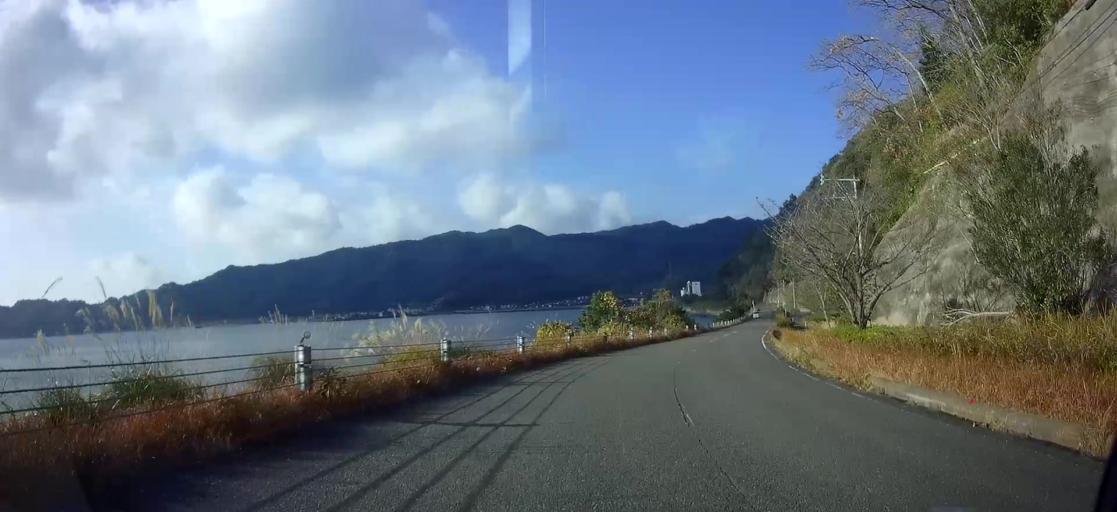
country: JP
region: Kumamoto
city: Minamata
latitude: 32.3831
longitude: 130.3797
